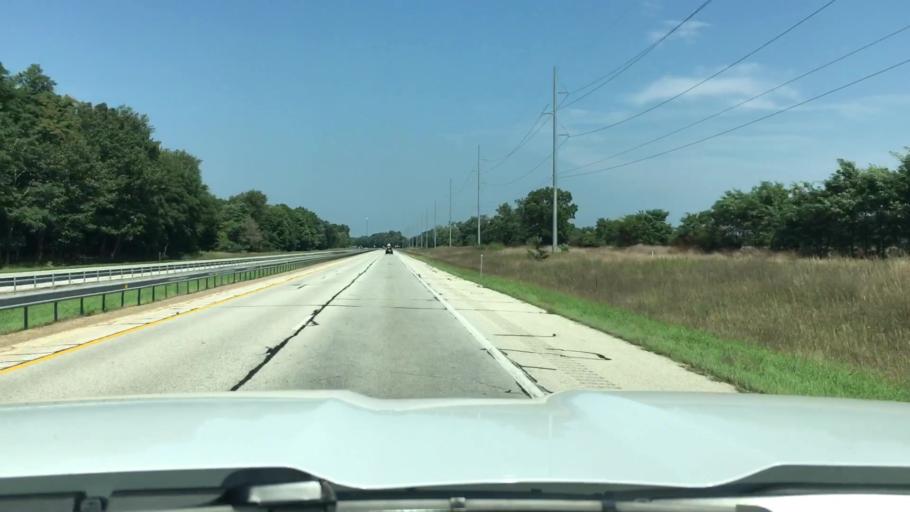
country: US
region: Michigan
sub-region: Saint Joseph County
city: Three Rivers
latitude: 42.0048
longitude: -85.6334
